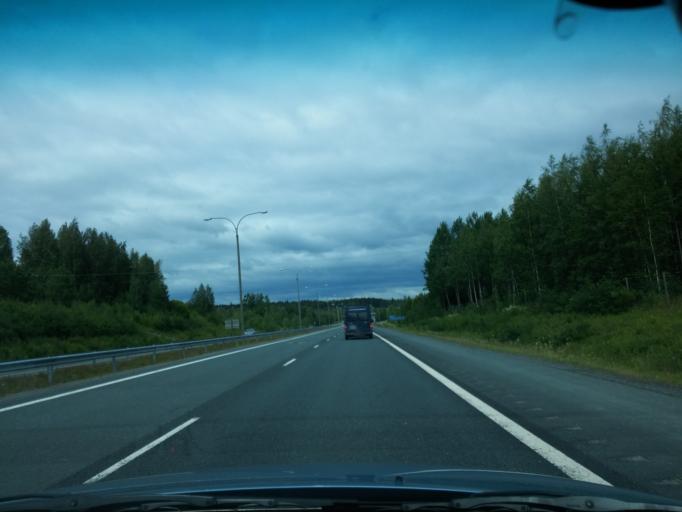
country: FI
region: Northern Savo
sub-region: Kuopio
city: Kuopio
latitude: 62.7921
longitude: 27.5943
